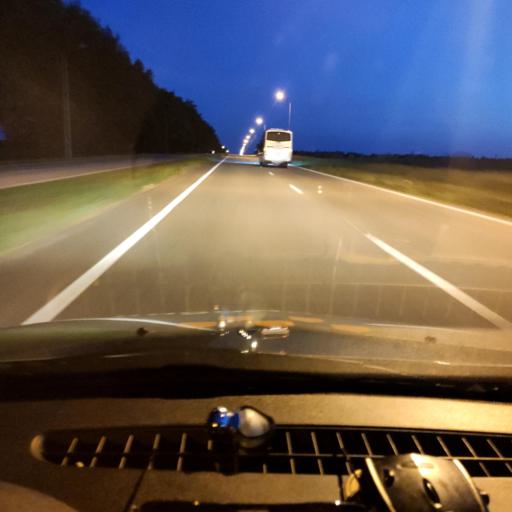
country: RU
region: Belgorod
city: Skorodnoye
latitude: 51.1512
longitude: 37.2885
